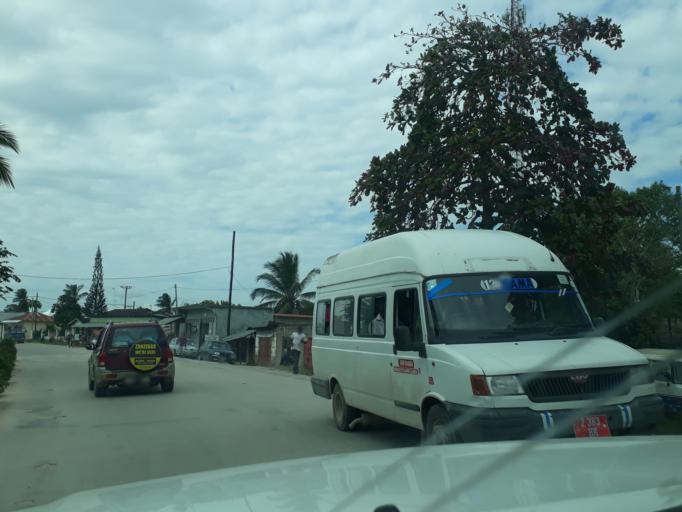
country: TZ
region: Zanzibar Central/South
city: Koani
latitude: -6.0898
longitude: 39.2216
